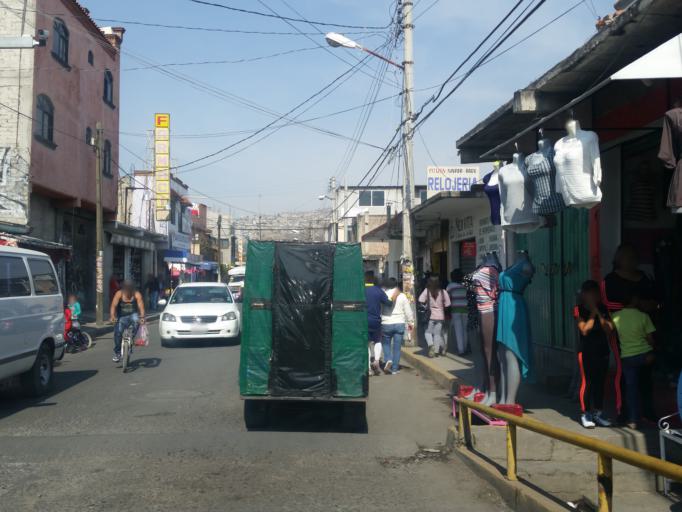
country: MX
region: Mexico
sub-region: La Paz
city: San Isidro
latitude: 19.3252
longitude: -98.9497
